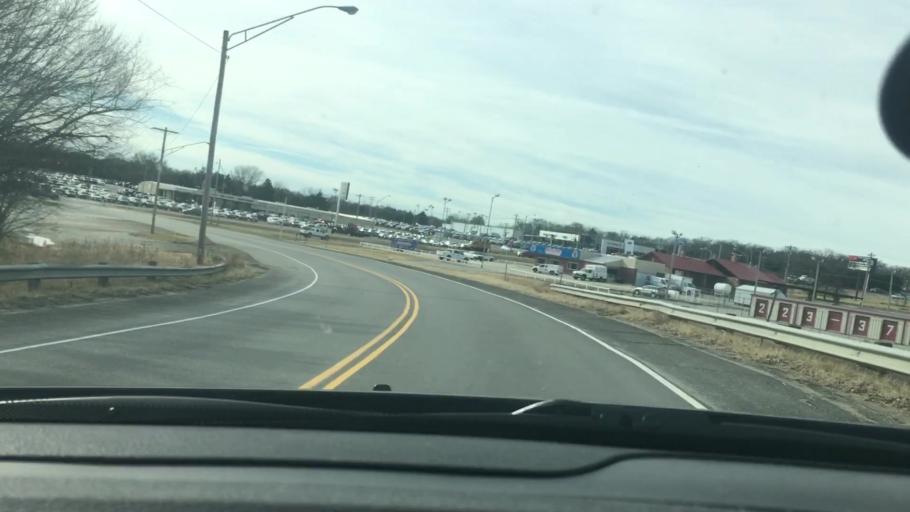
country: US
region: Oklahoma
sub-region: Carter County
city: Ardmore
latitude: 34.1744
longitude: -97.1761
